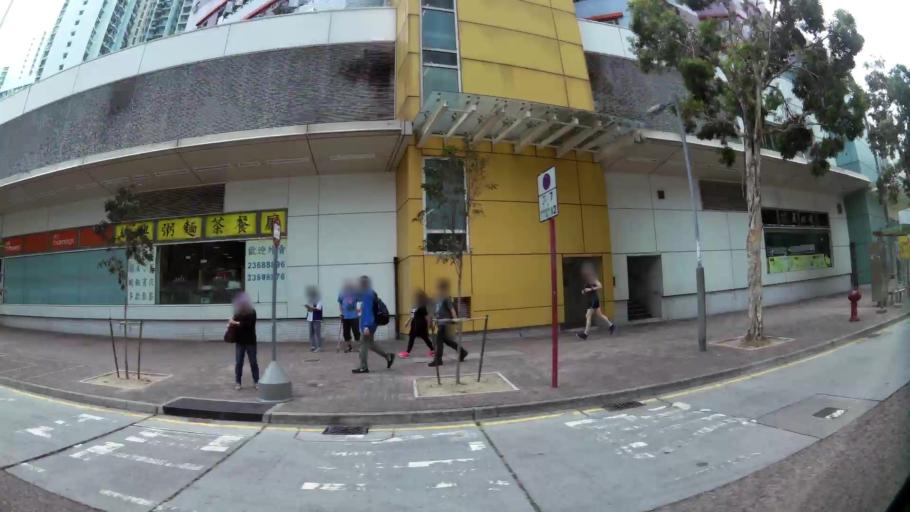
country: HK
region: Sham Shui Po
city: Sham Shui Po
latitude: 22.3273
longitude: 114.1548
